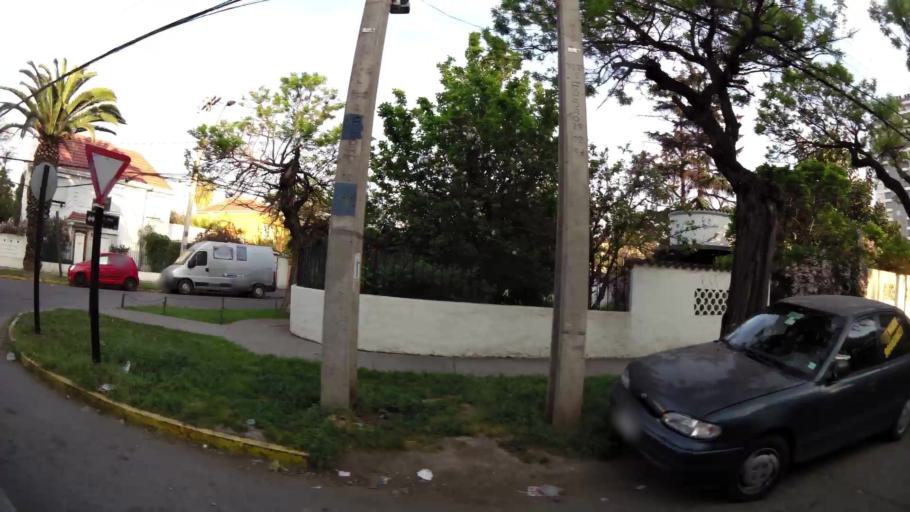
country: CL
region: Santiago Metropolitan
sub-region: Provincia de Santiago
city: Villa Presidente Frei, Nunoa, Santiago, Chile
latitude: -33.4561
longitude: -70.5767
